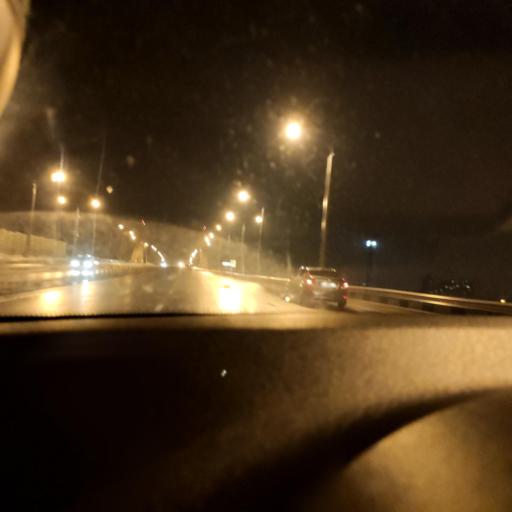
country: RU
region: Samara
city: Samara
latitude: 53.1714
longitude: 50.0862
